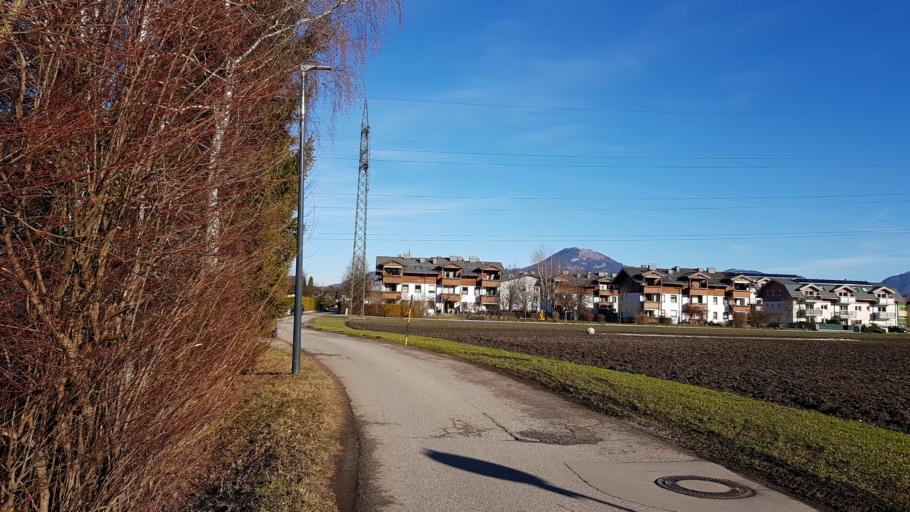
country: DE
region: Bavaria
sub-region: Upper Bavaria
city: Ainring
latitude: 47.7769
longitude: 12.9857
